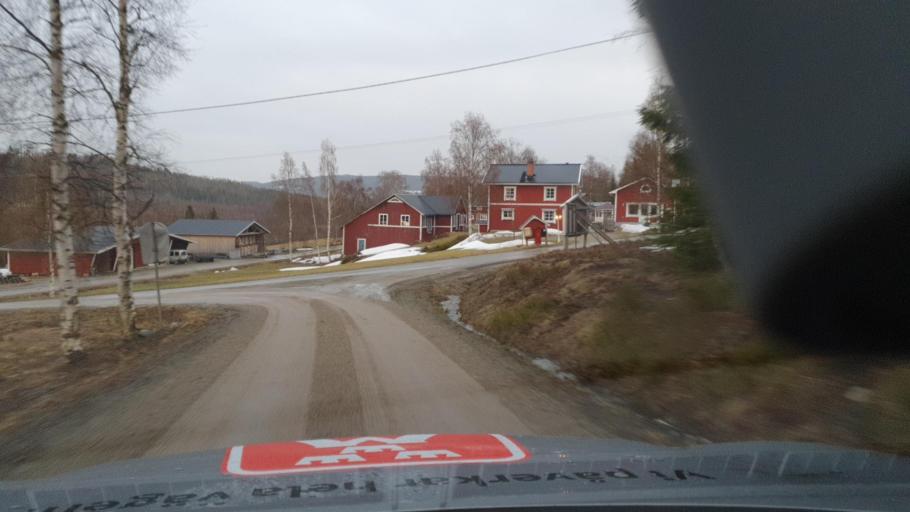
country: SE
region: Vaesternorrland
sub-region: OErnskoeldsviks Kommun
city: Bjasta
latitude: 63.2187
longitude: 18.2942
